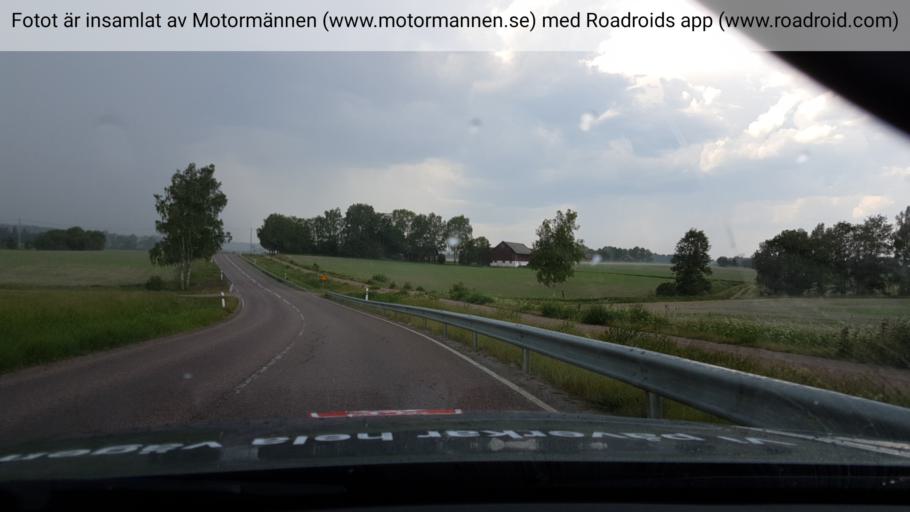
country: SE
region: Vaestmanland
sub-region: Vasteras
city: Skultuna
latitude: 59.6854
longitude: 16.4571
